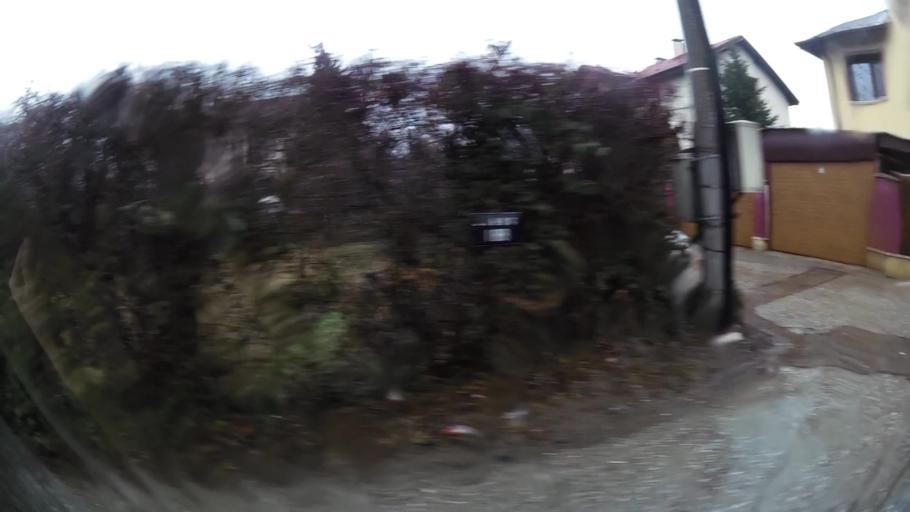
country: BG
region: Sofia-Capital
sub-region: Stolichna Obshtina
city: Sofia
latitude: 42.6262
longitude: 23.3617
